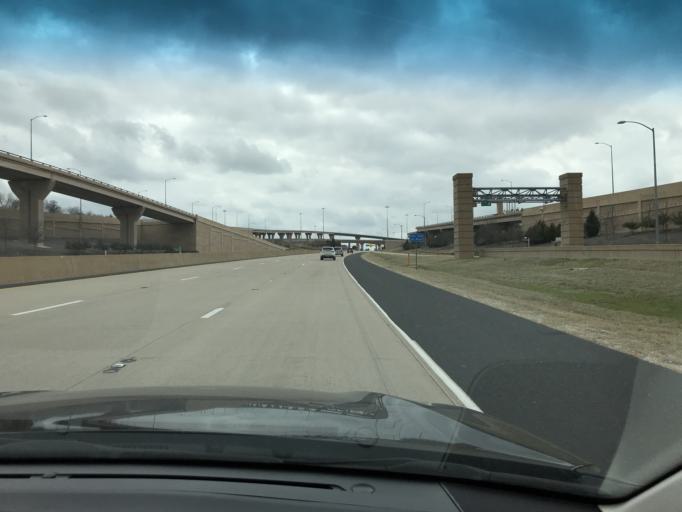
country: US
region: Texas
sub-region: Tarrant County
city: Benbrook
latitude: 32.6913
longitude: -97.4047
